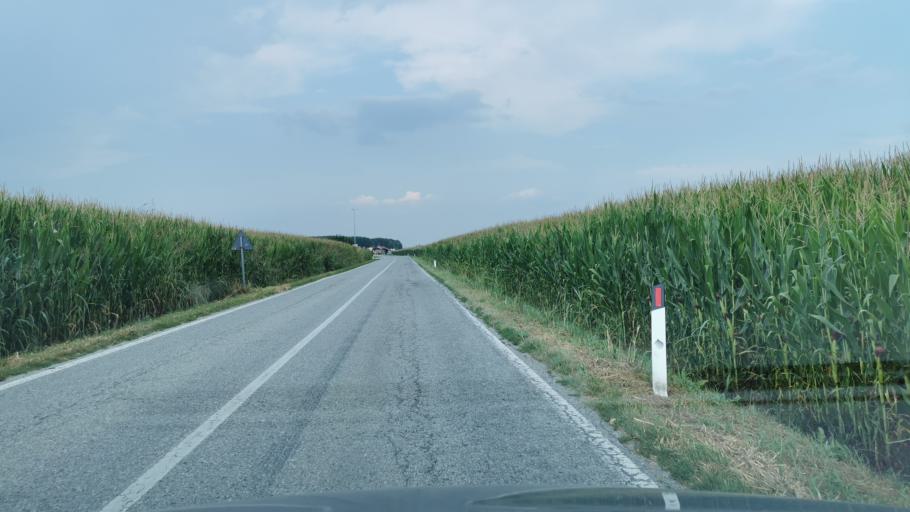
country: IT
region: Piedmont
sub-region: Provincia di Cuneo
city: Vottignasco
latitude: 44.5677
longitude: 7.5887
